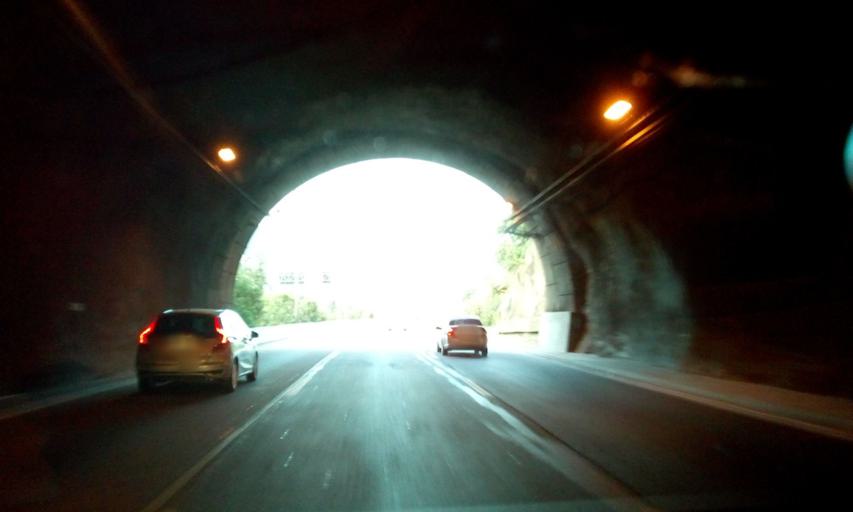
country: BR
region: Rio de Janeiro
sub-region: Sao Joao De Meriti
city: Sao Joao de Meriti
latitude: -22.9343
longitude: -43.3462
